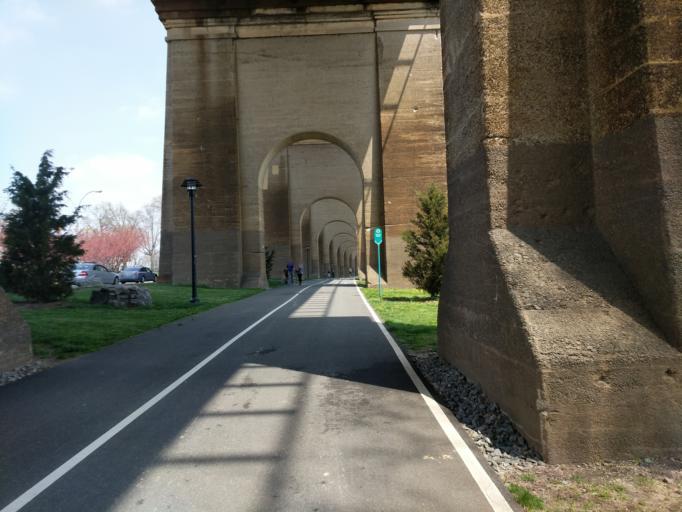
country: US
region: New York
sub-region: New York County
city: Manhattan
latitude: 40.7949
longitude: -73.9202
